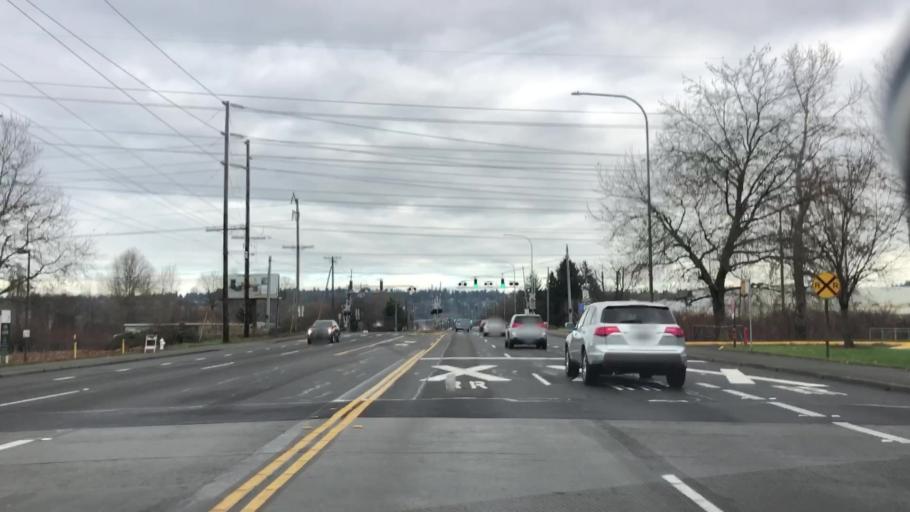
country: US
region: Washington
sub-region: King County
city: Kent
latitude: 47.4122
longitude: -122.2433
